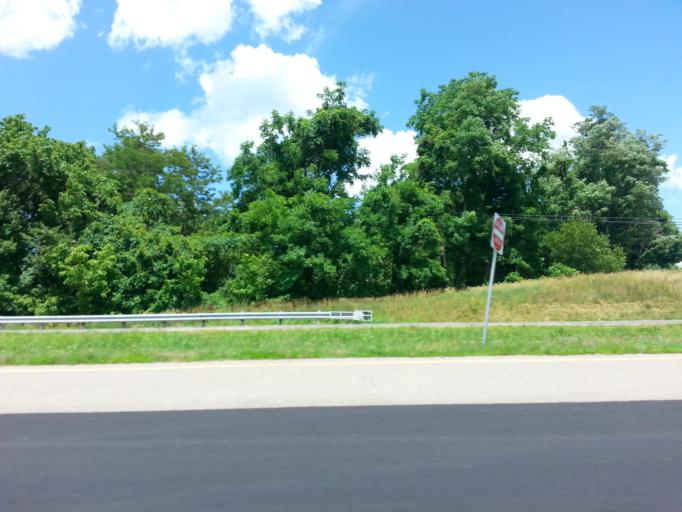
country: US
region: Virginia
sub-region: Lee County
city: Jonesville
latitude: 36.6893
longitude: -83.2304
